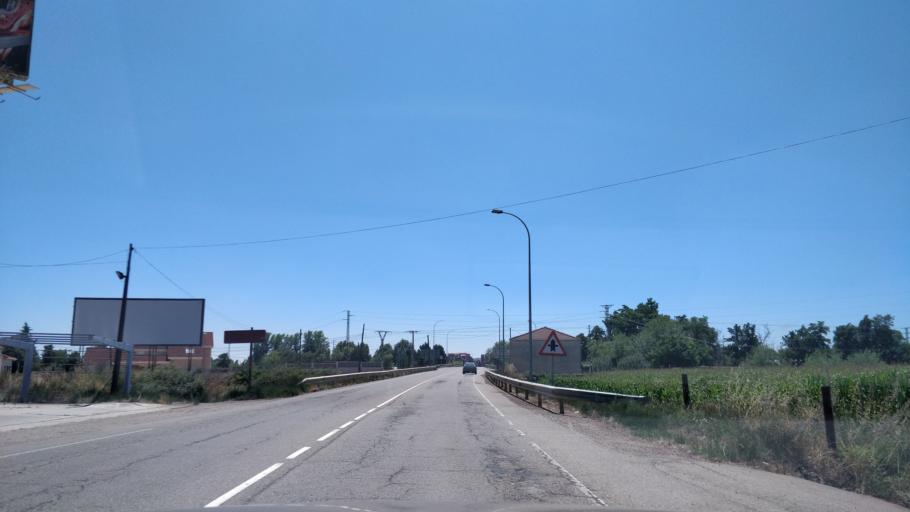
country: ES
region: Castille and Leon
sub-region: Provincia de Leon
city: La Baneza
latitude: 42.3106
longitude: -5.8931
